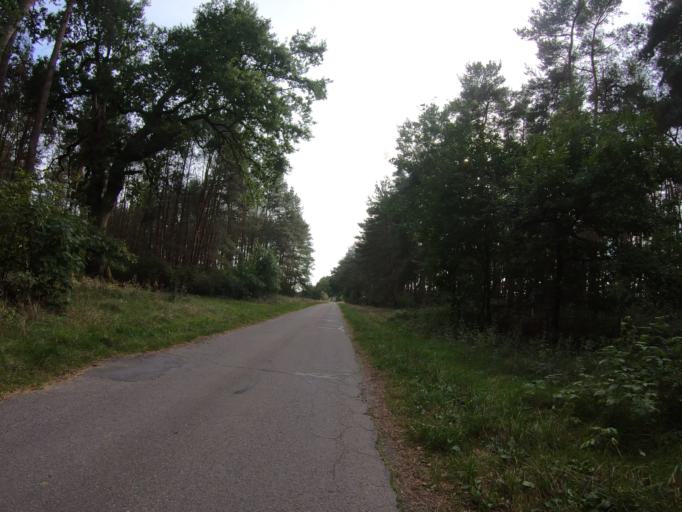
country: DE
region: Lower Saxony
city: Ribbesbuttel
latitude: 52.4433
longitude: 10.5167
